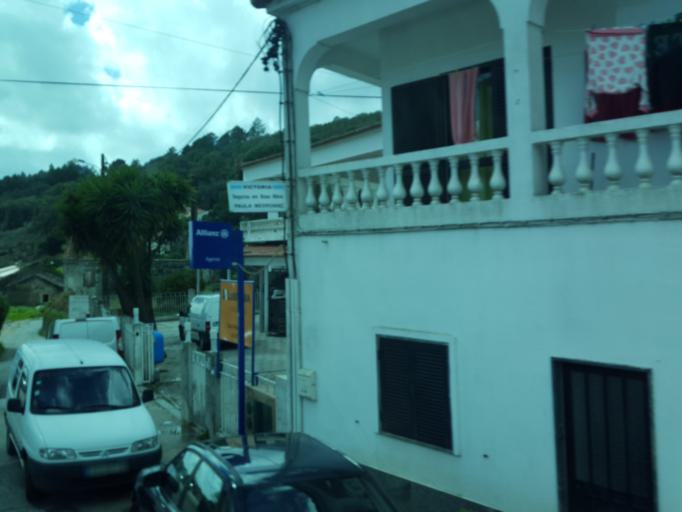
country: PT
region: Faro
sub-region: Monchique
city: Monchique
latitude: 37.3119
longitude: -8.5558
